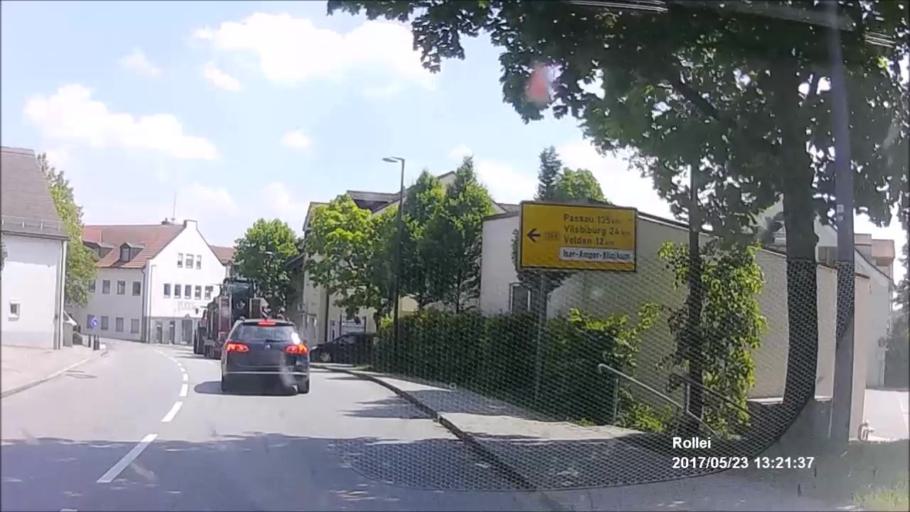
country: DE
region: Bavaria
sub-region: Upper Bavaria
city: Taufkirchen
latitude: 48.3469
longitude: 12.1307
